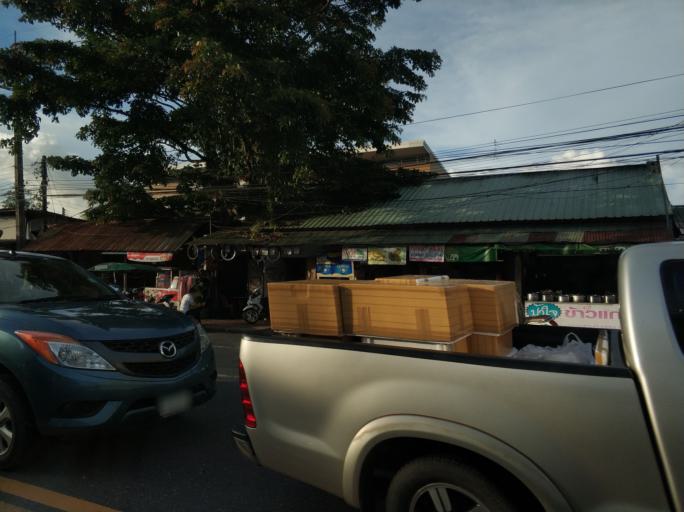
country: TH
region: Phuket
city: Kathu
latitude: 7.8998
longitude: 98.3505
